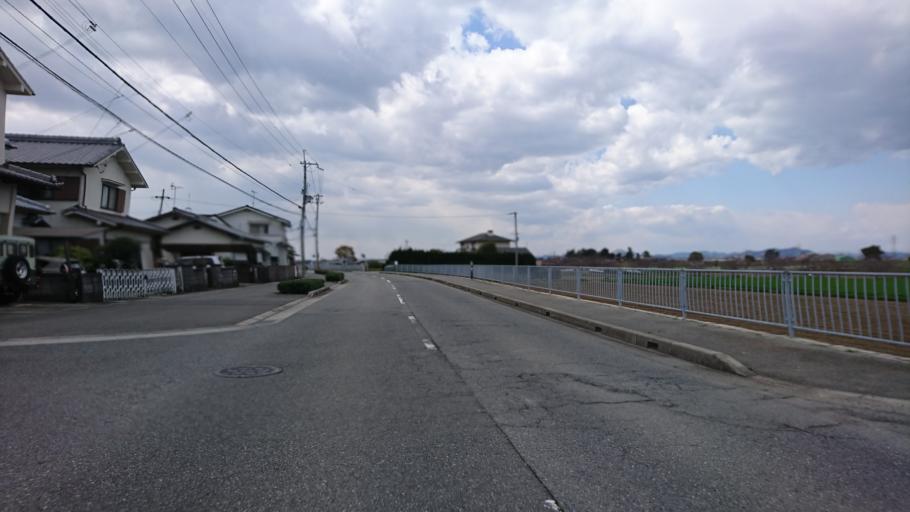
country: JP
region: Hyogo
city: Kakogawacho-honmachi
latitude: 34.7538
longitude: 134.9089
